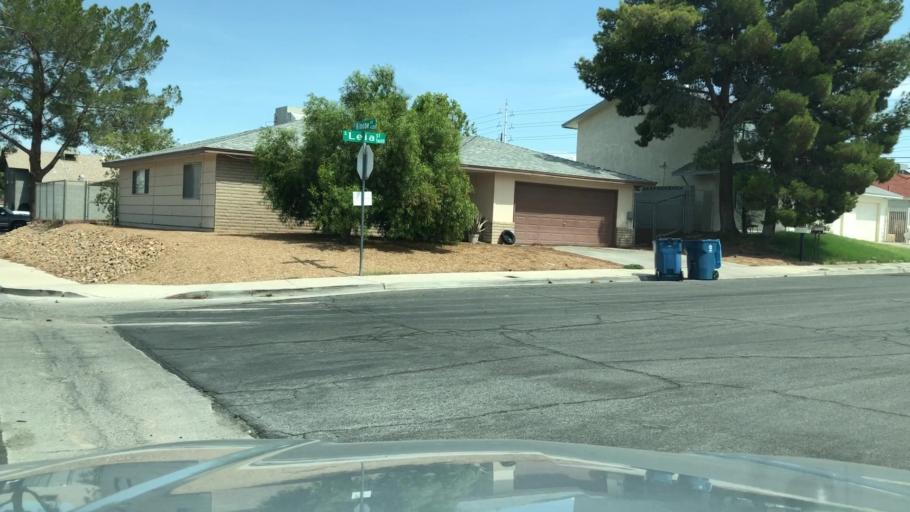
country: US
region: Nevada
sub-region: Clark County
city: Whitney
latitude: 36.0864
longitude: -115.0799
